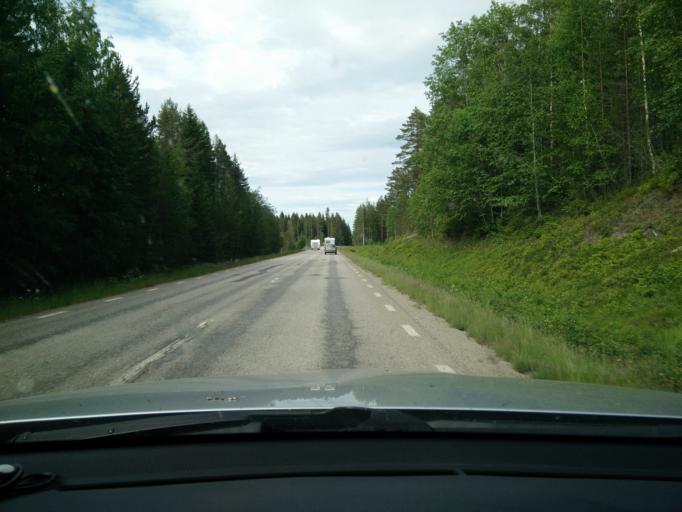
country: SE
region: Gaevleborg
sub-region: Nordanstigs Kommun
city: Bergsjoe
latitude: 61.9337
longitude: 17.0383
